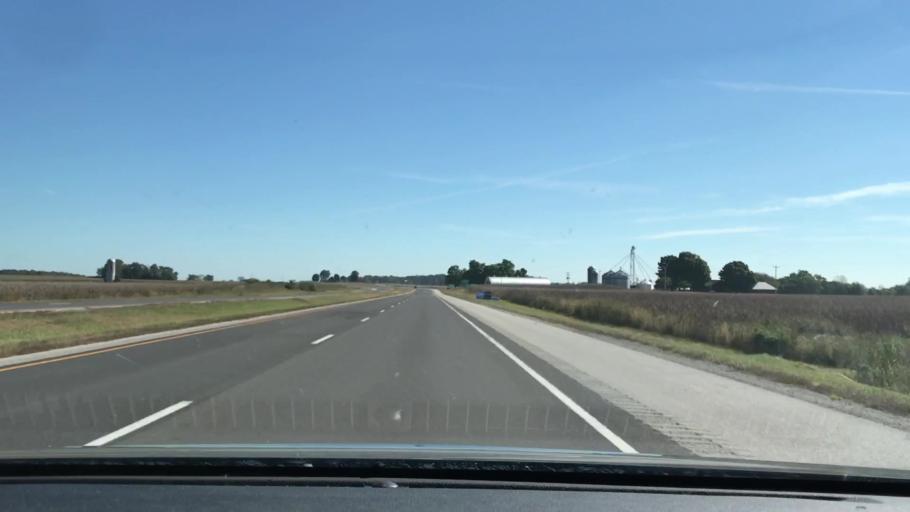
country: US
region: Kentucky
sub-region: Todd County
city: Elkton
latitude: 36.8052
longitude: -87.0599
